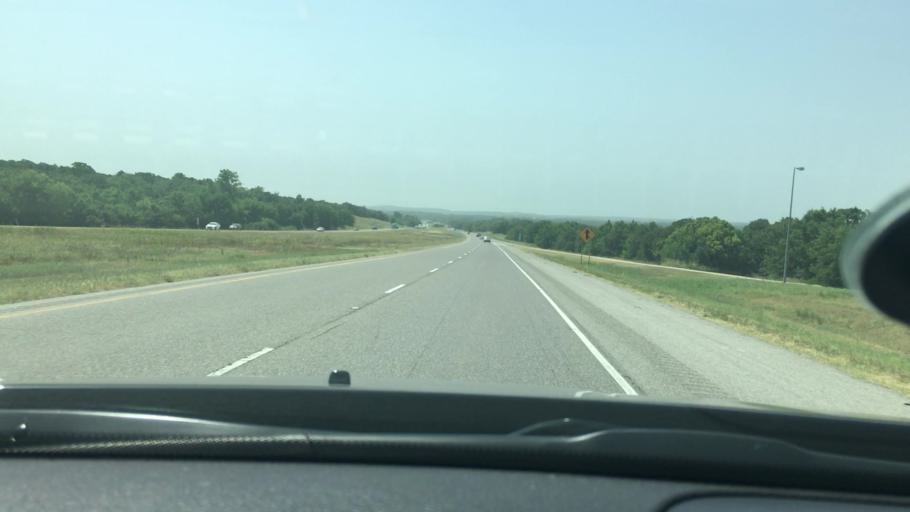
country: US
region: Oklahoma
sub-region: Murray County
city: Davis
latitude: 34.5473
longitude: -97.1908
